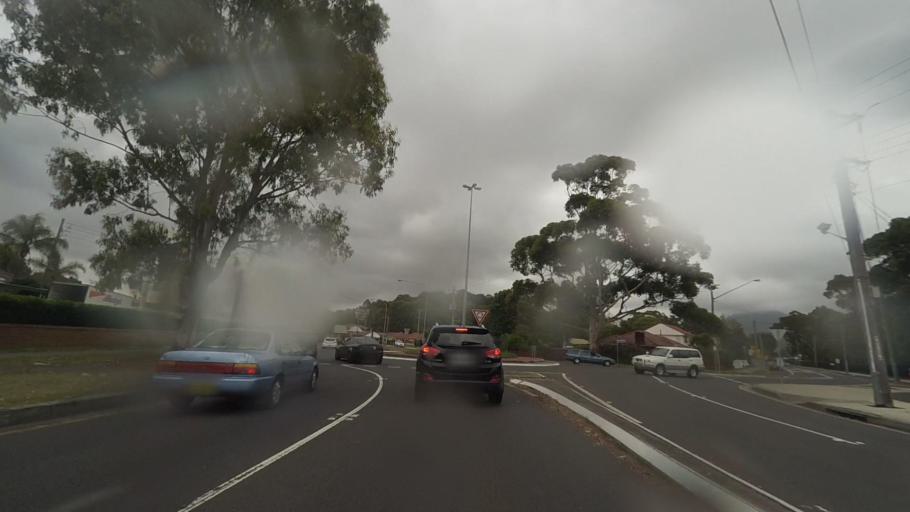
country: AU
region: New South Wales
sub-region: Wollongong
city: Mangerton
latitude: -34.4398
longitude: 150.8568
